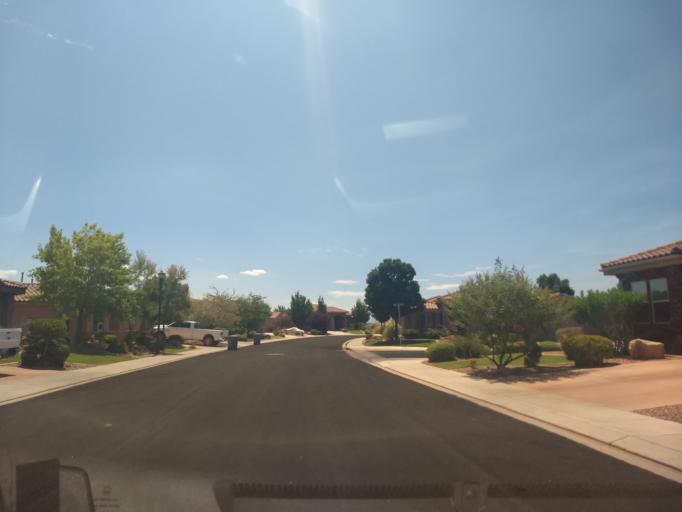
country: US
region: Utah
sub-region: Washington County
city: Washington
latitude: 37.1435
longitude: -113.4819
